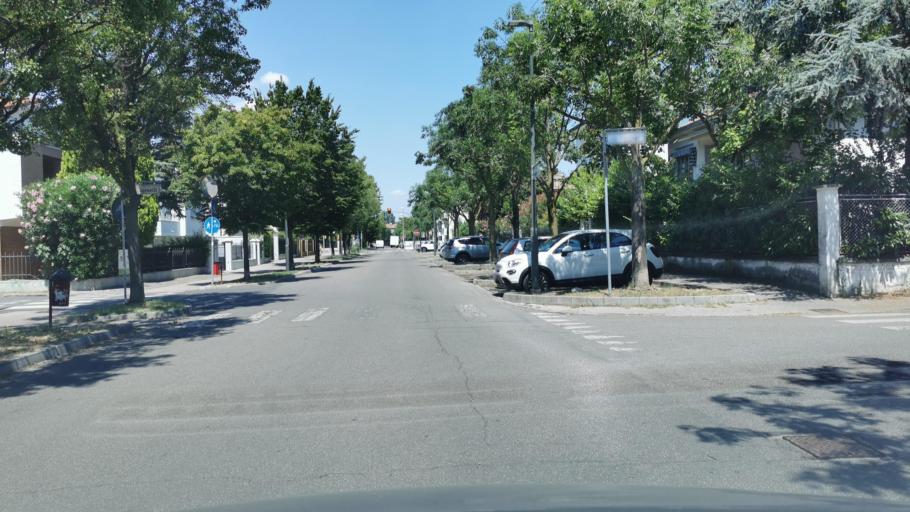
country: IT
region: Emilia-Romagna
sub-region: Provincia di Modena
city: Carpi Centro
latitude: 44.7880
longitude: 10.8856
